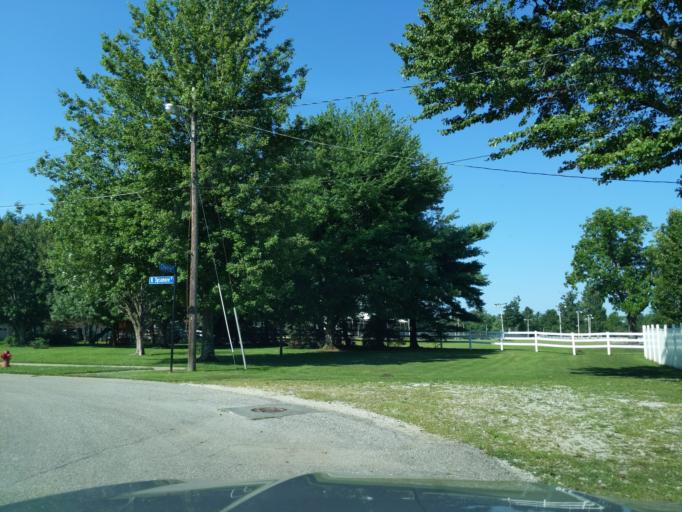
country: US
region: Indiana
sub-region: Ripley County
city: Osgood
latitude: 39.1324
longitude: -85.2960
